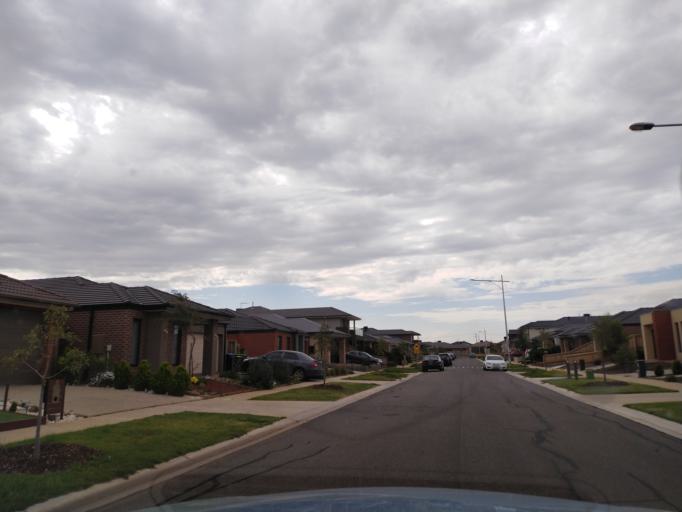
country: AU
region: Victoria
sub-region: Wyndham
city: Williams Landing
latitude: -37.8395
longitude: 144.7129
